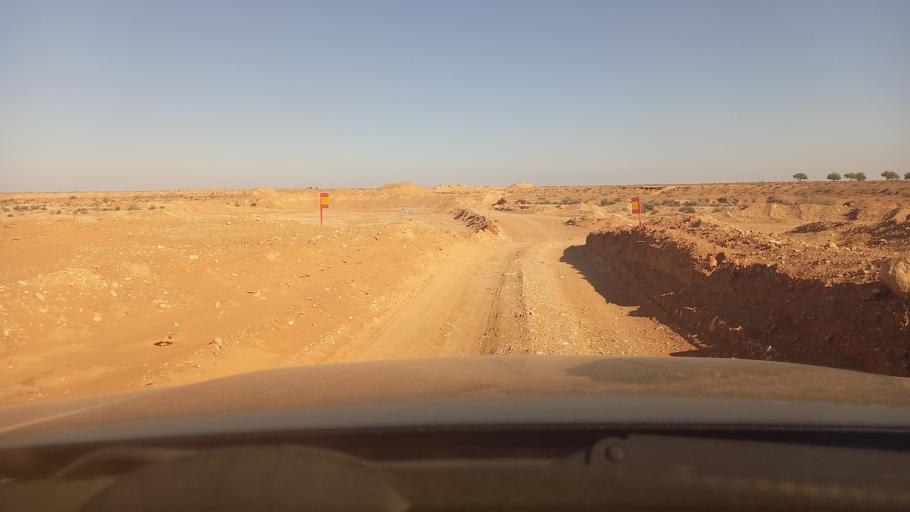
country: TN
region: Madanin
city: Medenine
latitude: 33.1470
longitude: 10.5070
